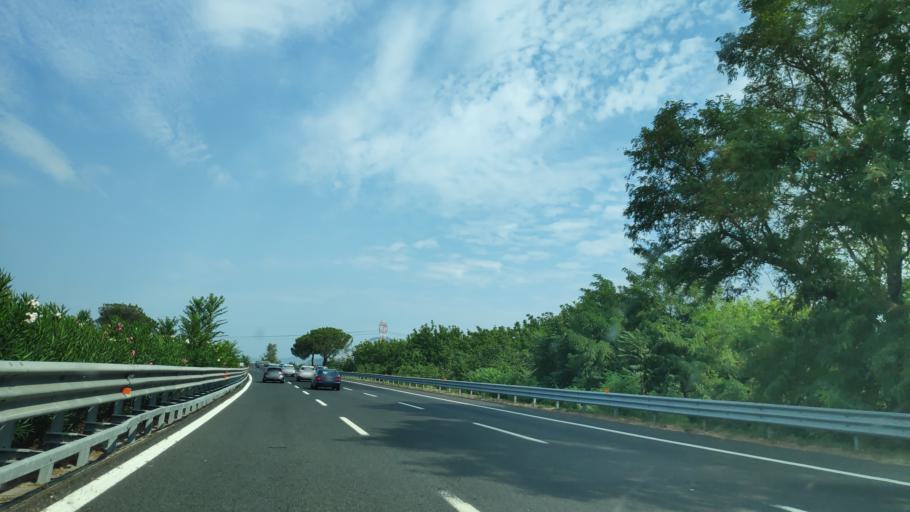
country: IT
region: Campania
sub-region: Provincia di Caserta
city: Montedecoro
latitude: 41.0028
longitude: 14.4058
